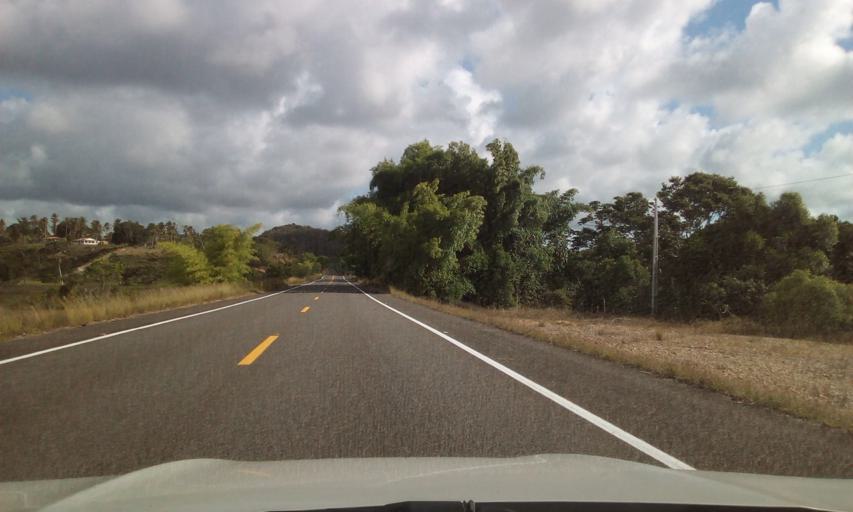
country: BR
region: Bahia
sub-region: Conde
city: Conde
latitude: -11.6964
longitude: -37.5713
